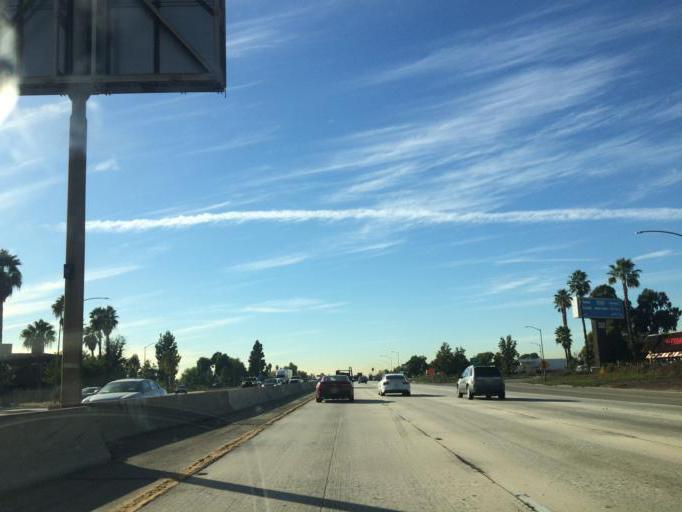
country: US
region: California
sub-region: Los Angeles County
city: Covina
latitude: 34.0720
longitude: -117.8872
